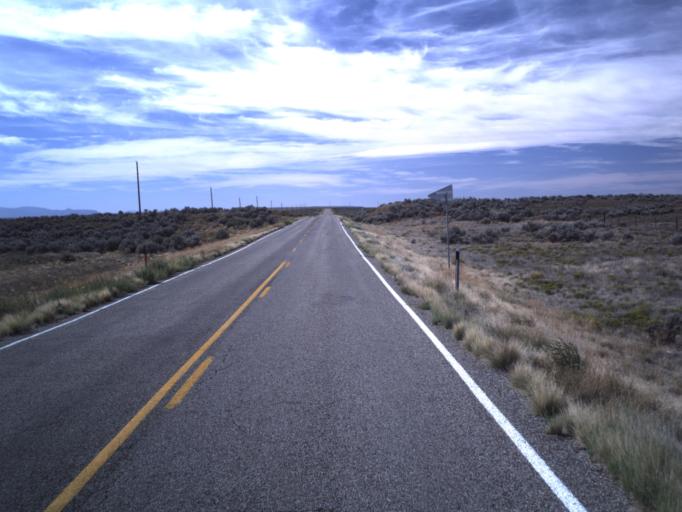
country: US
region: Utah
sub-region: San Juan County
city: Blanding
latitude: 37.4070
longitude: -109.3363
